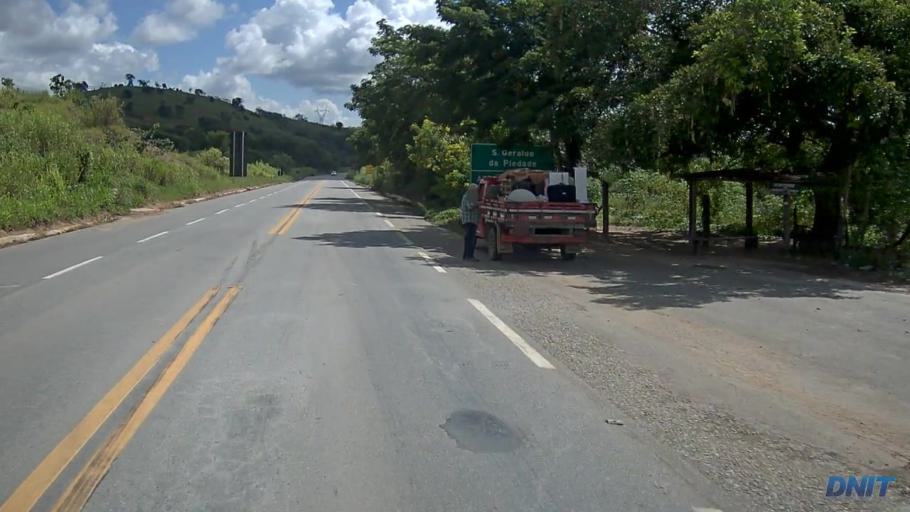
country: BR
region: Minas Gerais
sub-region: Governador Valadares
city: Governador Valadares
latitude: -19.0179
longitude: -42.1418
